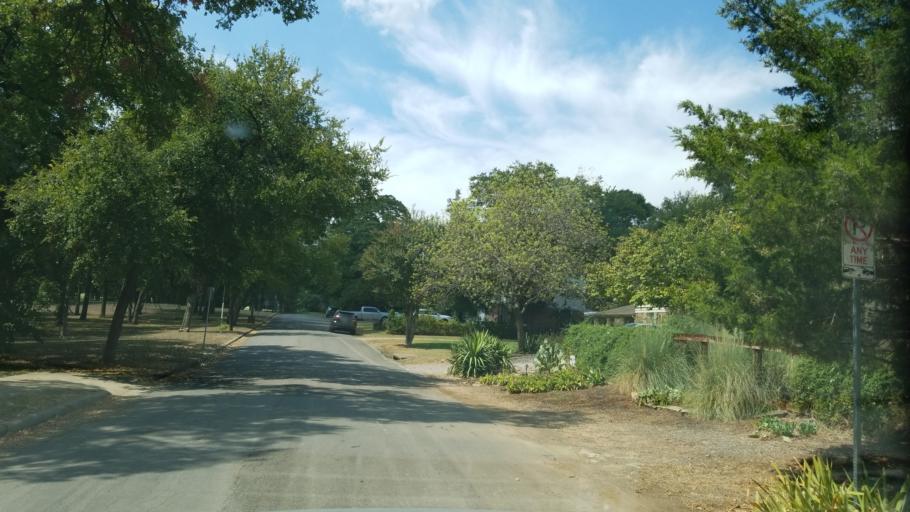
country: US
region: Texas
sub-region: Dallas County
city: Cockrell Hill
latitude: 32.7573
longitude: -96.8547
